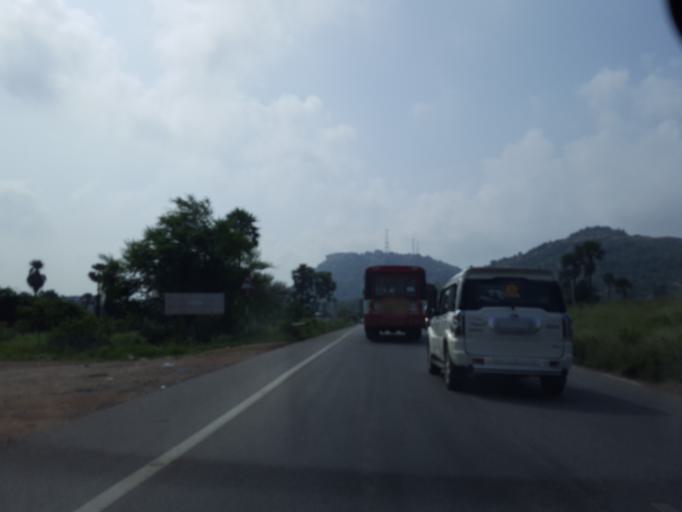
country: IN
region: Telangana
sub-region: Rangareddi
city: Ghatkesar
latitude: 17.2976
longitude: 78.7403
